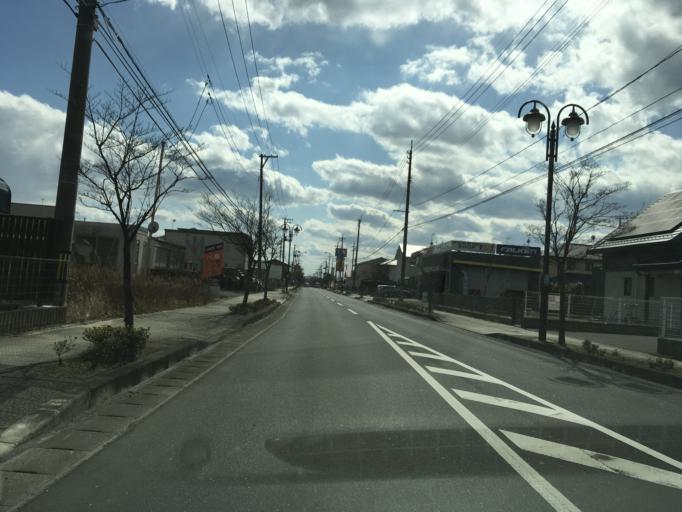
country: JP
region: Miyagi
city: Wakuya
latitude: 38.7025
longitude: 141.2126
